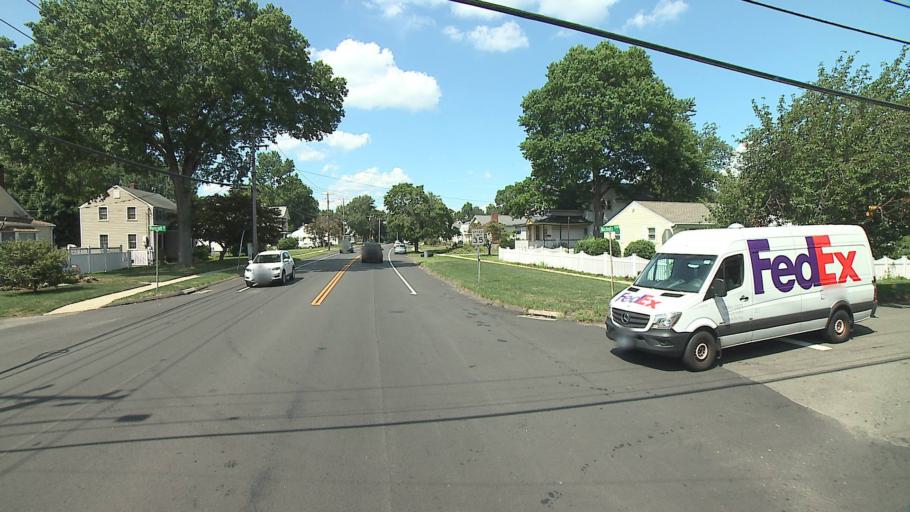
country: US
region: Connecticut
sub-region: Fairfield County
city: Stratford
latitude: 41.2053
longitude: -73.1424
